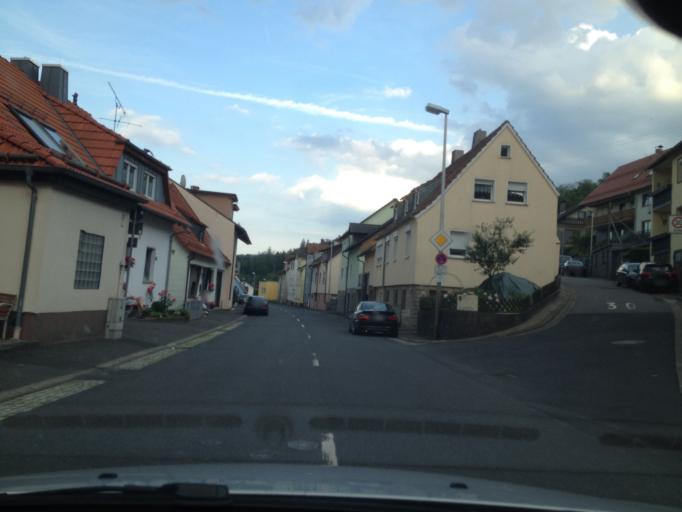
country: DE
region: Bavaria
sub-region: Regierungsbezirk Unterfranken
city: Weibersbrunn
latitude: 49.9287
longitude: 9.3709
